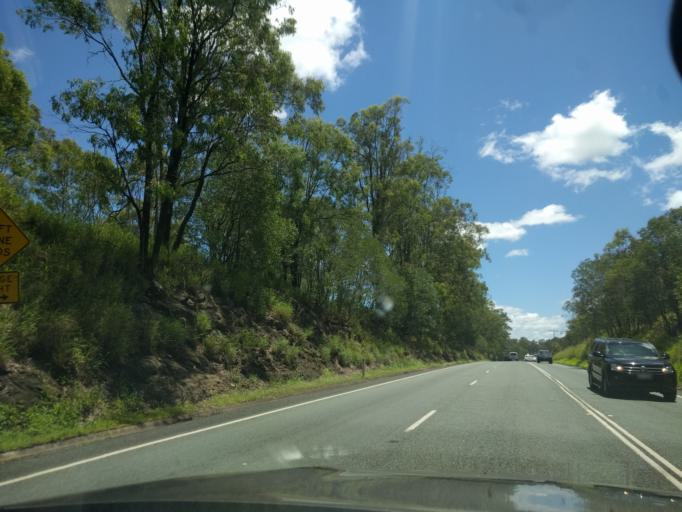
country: AU
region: Queensland
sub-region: Logan
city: Cedar Vale
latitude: -27.8406
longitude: 153.0241
